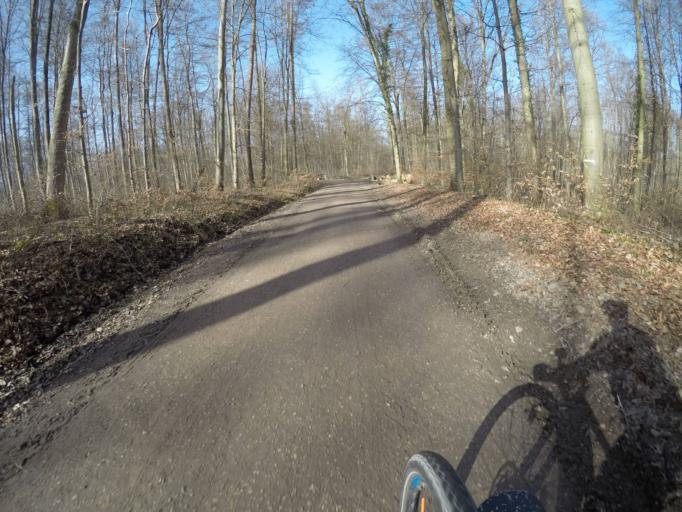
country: DE
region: Baden-Wuerttemberg
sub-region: Regierungsbezirk Stuttgart
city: Notzingen
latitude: 48.6784
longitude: 9.4674
